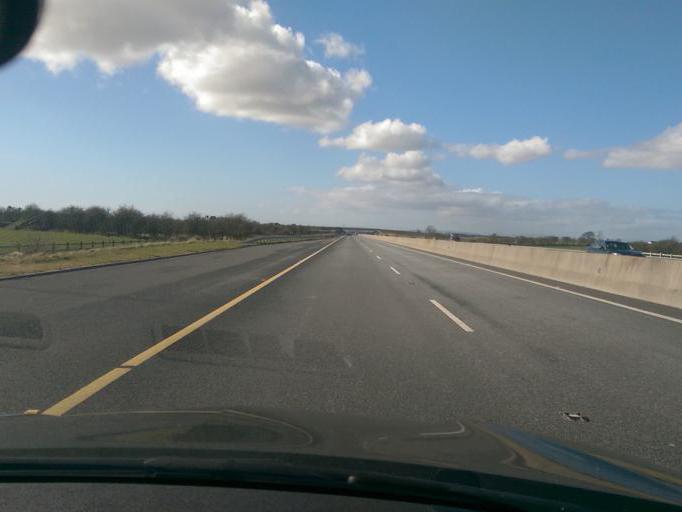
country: IE
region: Connaught
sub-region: County Galway
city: Athenry
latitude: 53.2984
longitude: -8.8299
